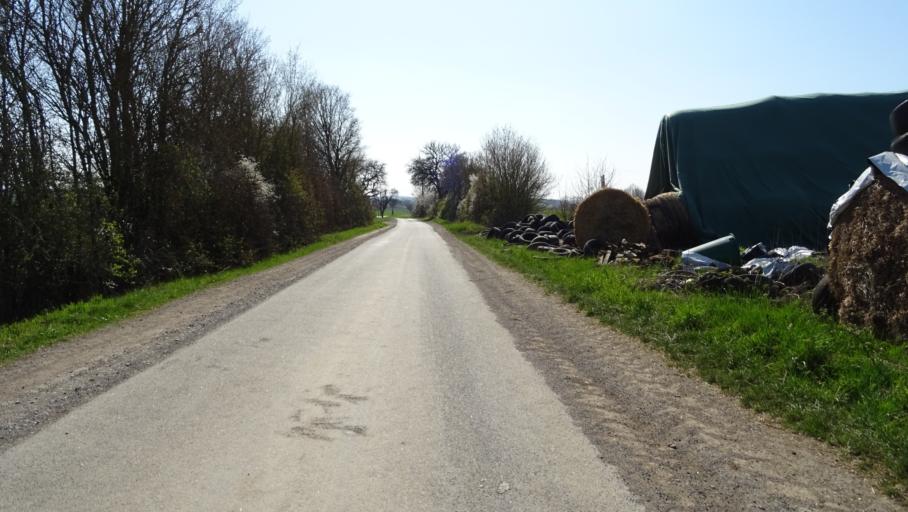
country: DE
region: Baden-Wuerttemberg
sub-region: Karlsruhe Region
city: Billigheim
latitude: 49.3864
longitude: 9.2292
